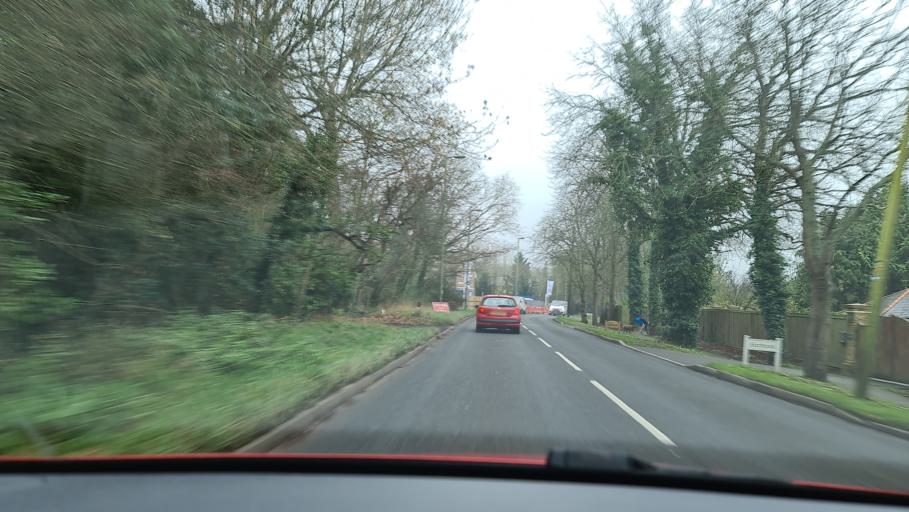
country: GB
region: England
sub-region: Surrey
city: Leatherhead
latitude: 51.3253
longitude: -0.3525
